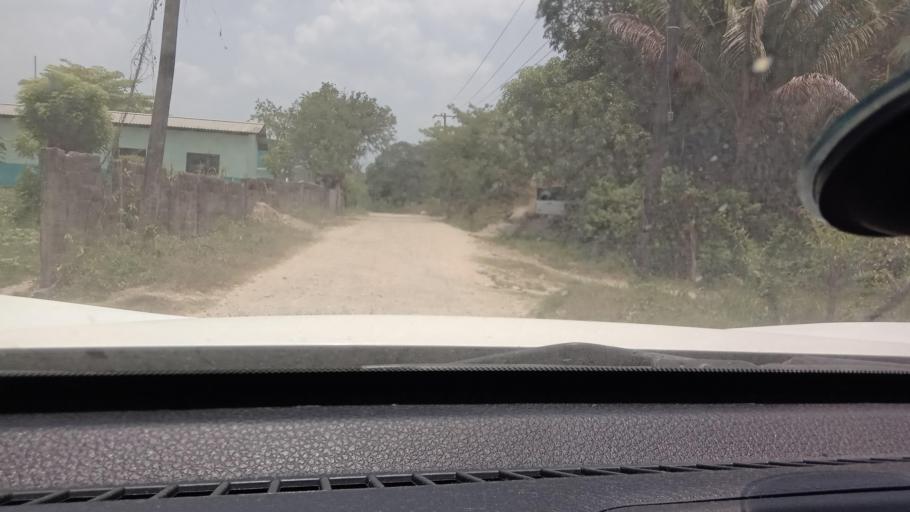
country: MX
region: Tabasco
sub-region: Huimanguillo
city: Francisco Rueda
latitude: 17.5040
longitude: -93.9024
